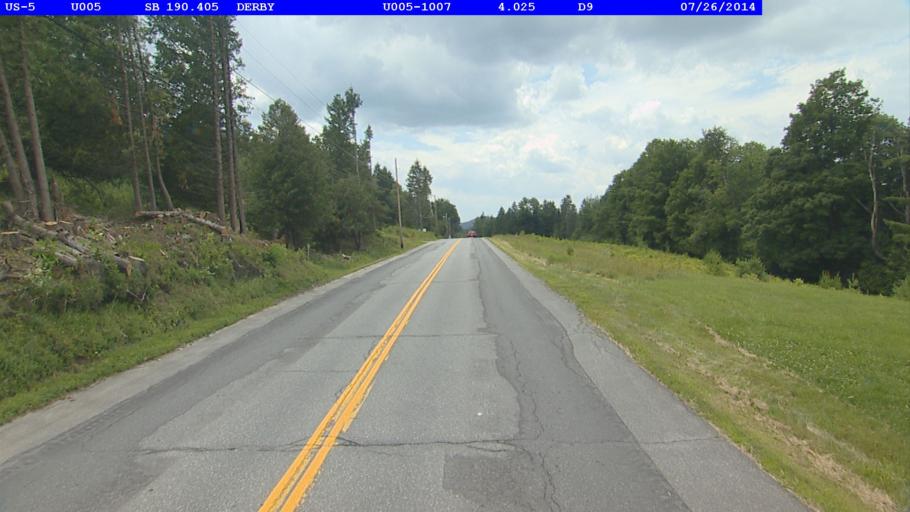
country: US
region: Vermont
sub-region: Orleans County
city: Newport
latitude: 44.9804
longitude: -72.1117
